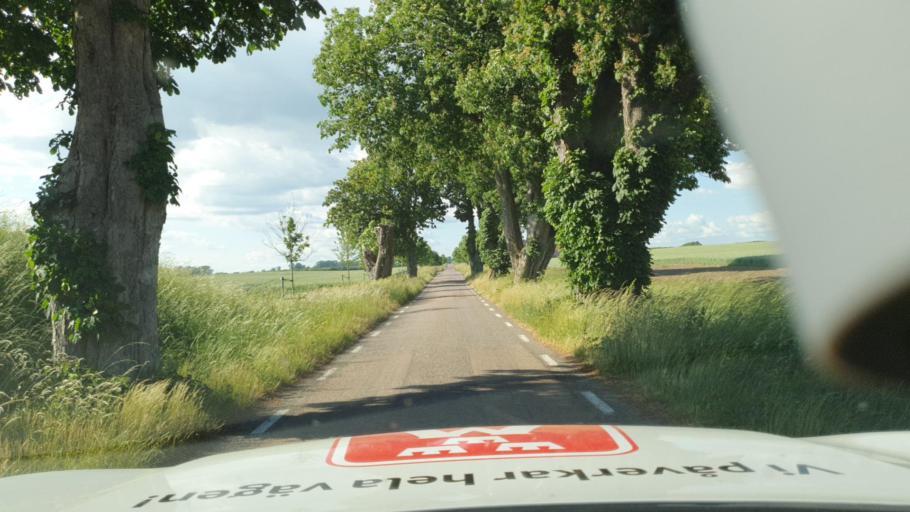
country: SE
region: Skane
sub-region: Ystads Kommun
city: Ystad
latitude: 55.4290
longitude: 13.7389
